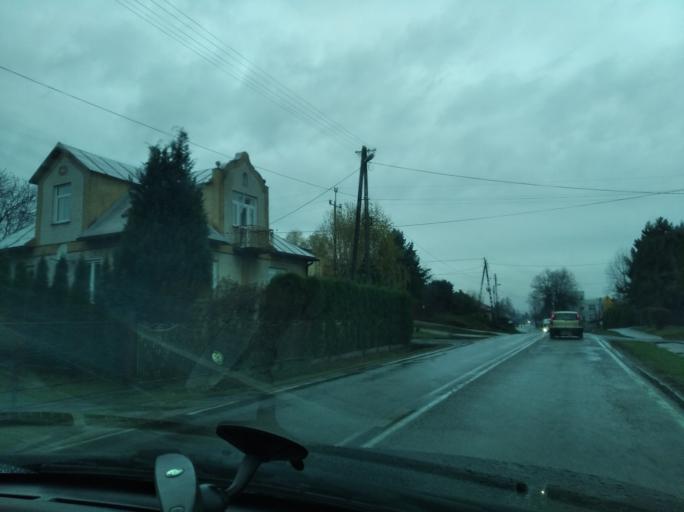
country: PL
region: Subcarpathian Voivodeship
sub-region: Powiat lancucki
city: Albigowa
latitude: 50.0156
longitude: 22.2248
